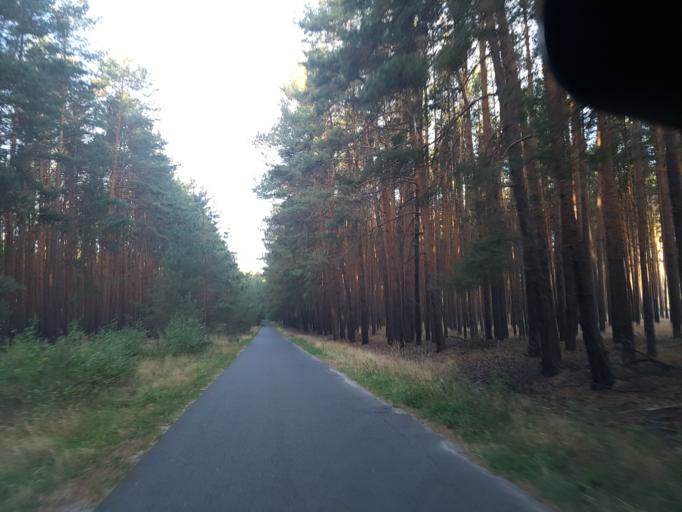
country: DE
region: Brandenburg
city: Hohenbucko
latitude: 51.7409
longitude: 13.5077
